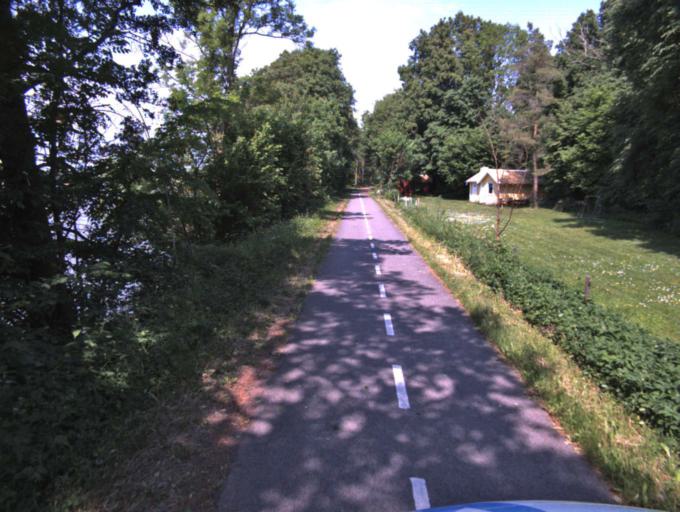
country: SE
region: Skane
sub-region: Kristianstads Kommun
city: Fjalkinge
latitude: 56.0903
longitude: 14.2333
